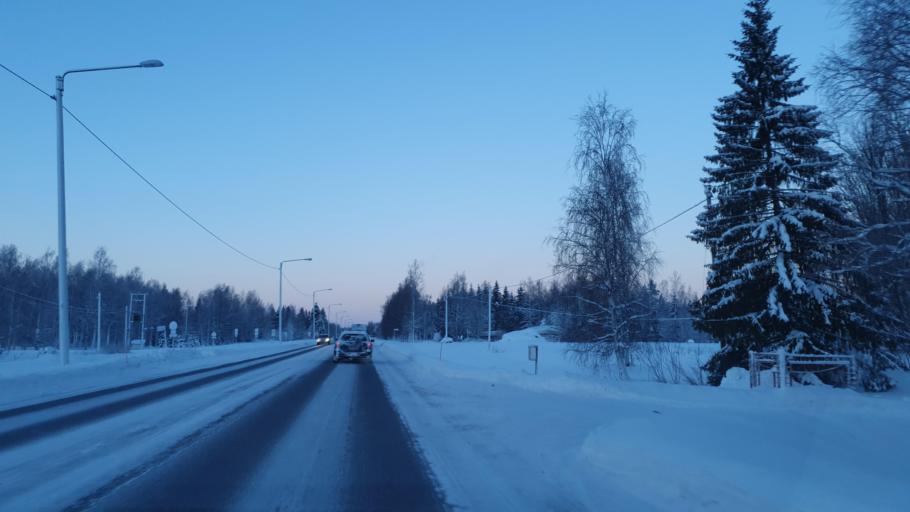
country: FI
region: Lapland
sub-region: Kemi-Tornio
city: Tornio
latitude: 65.8811
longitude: 24.1537
